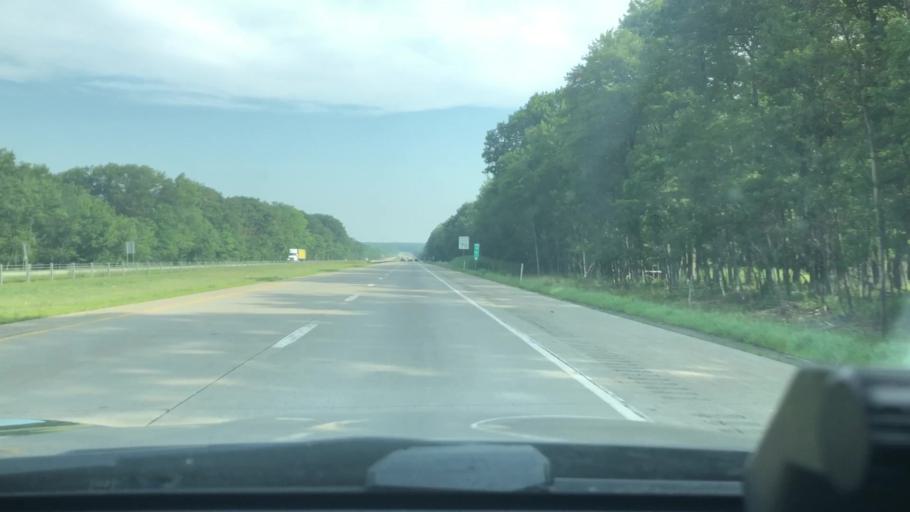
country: US
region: Pennsylvania
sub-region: Monroe County
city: Emerald Lakes
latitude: 41.1122
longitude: -75.3982
